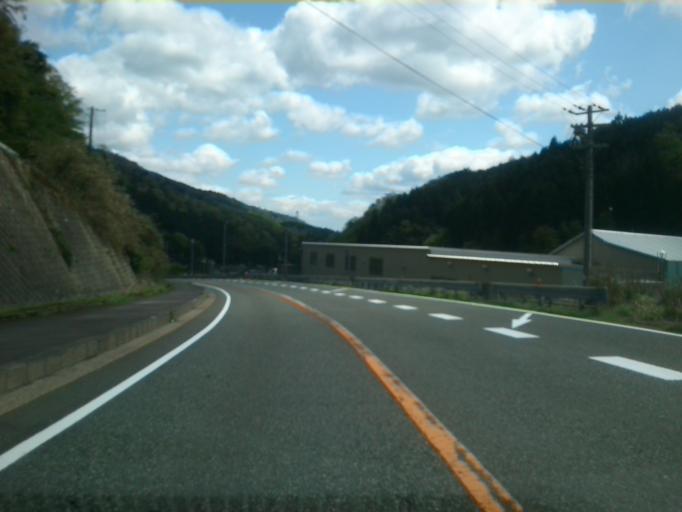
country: JP
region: Kyoto
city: Fukuchiyama
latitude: 35.4159
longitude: 135.0389
